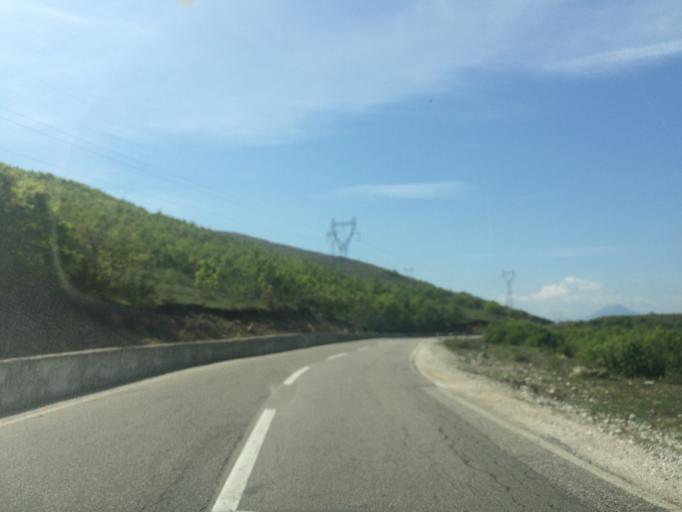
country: XK
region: Gjakova
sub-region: Komuna e Junikut
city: Junik
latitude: 42.4107
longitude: 20.2123
